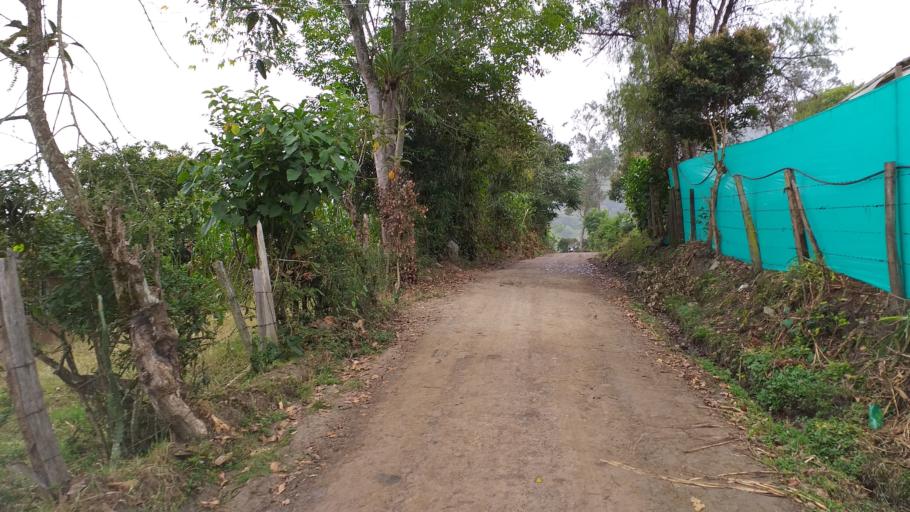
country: CO
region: Cundinamarca
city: Tenza
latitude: 5.0908
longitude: -73.4540
